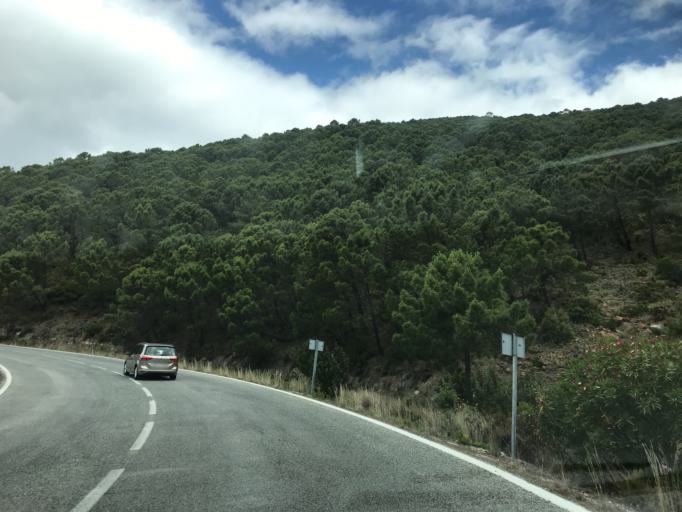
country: ES
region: Andalusia
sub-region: Provincia de Malaga
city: Benahavis
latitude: 36.5592
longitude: -5.0528
